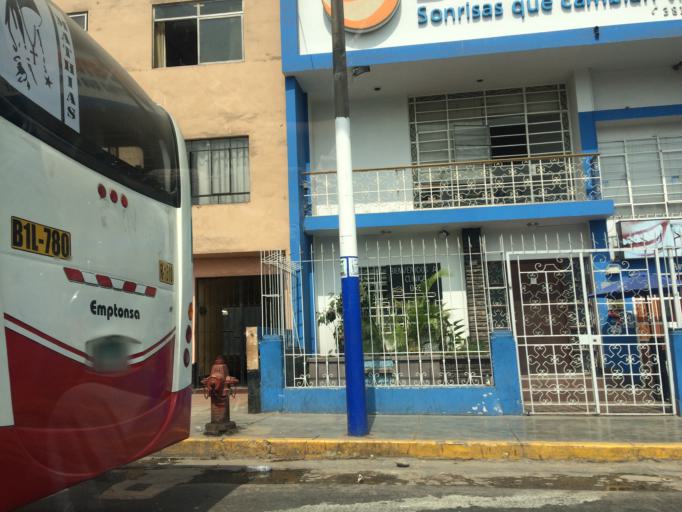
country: PE
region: Lima
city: Lima
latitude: -12.0262
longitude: -77.0344
